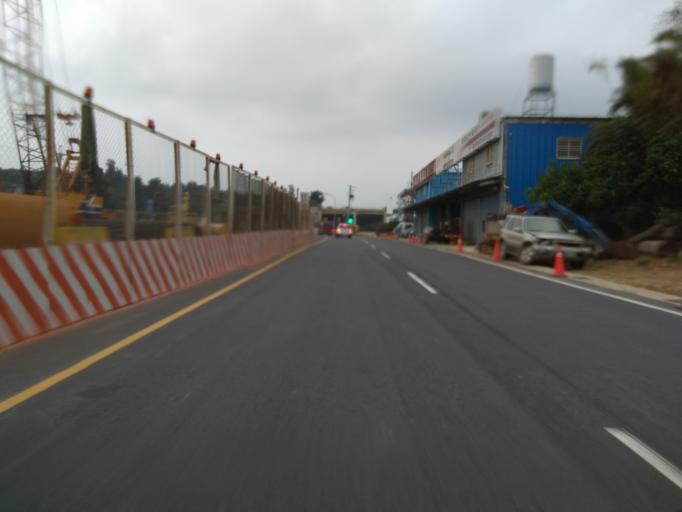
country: TW
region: Taiwan
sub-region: Hsinchu
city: Zhubei
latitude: 24.8966
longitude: 120.9657
